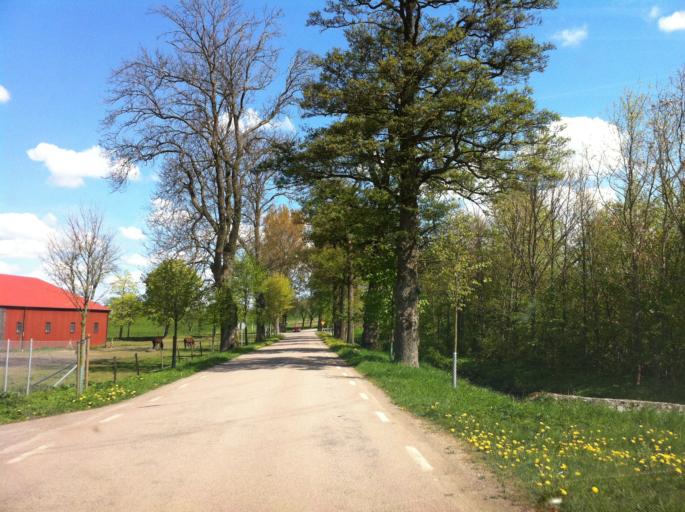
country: SE
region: Skane
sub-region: Landskrona
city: Asmundtorp
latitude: 55.9260
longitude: 12.9985
